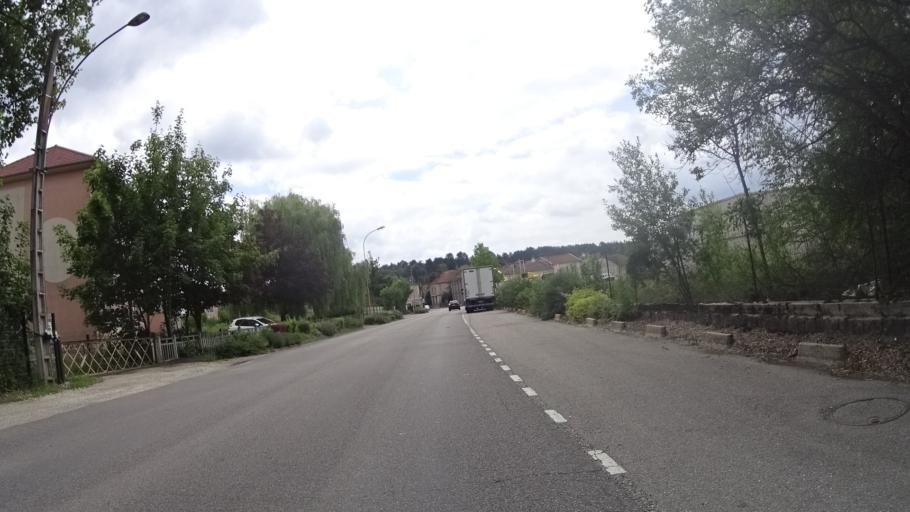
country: FR
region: Lorraine
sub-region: Departement de la Meuse
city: Lerouville
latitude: 48.7950
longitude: 5.5405
